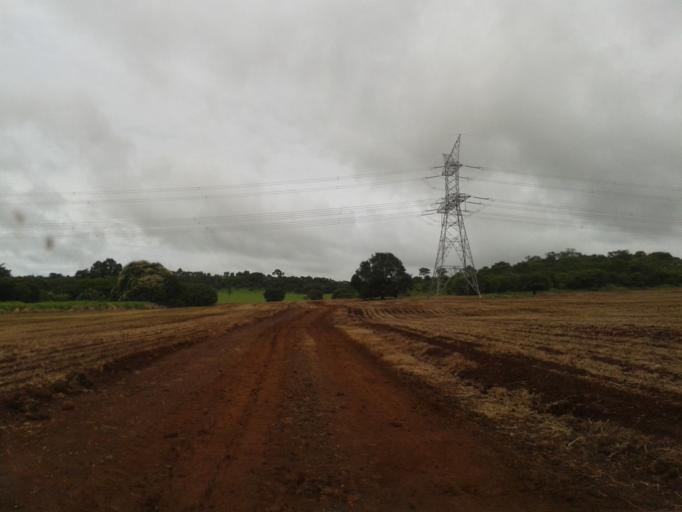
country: BR
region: Minas Gerais
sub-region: Capinopolis
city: Capinopolis
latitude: -18.7274
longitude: -49.7723
